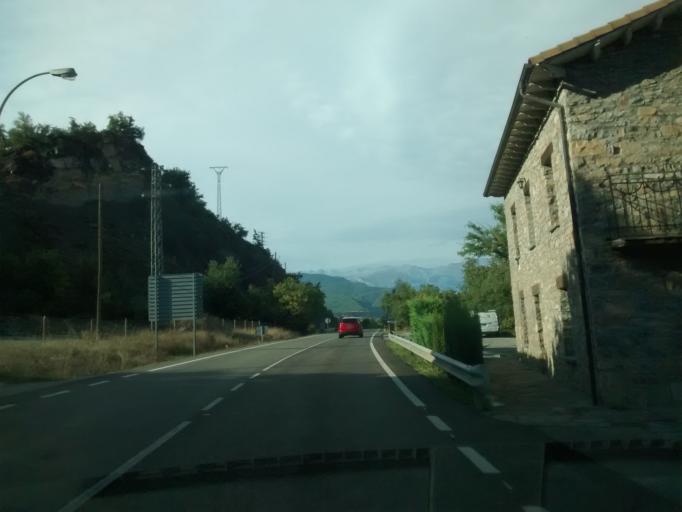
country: ES
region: Aragon
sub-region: Provincia de Huesca
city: Ainsa
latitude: 42.4182
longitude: 0.1401
